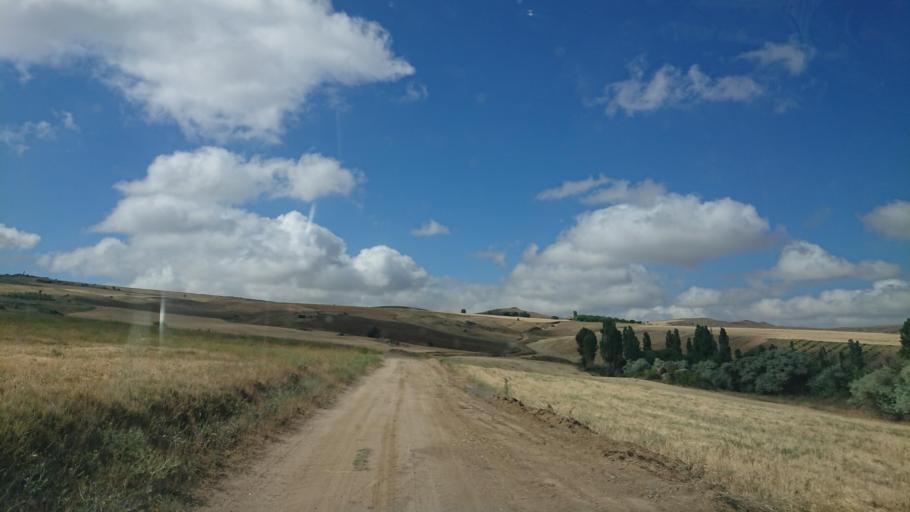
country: TR
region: Aksaray
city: Agacoren
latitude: 38.8514
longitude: 33.9395
